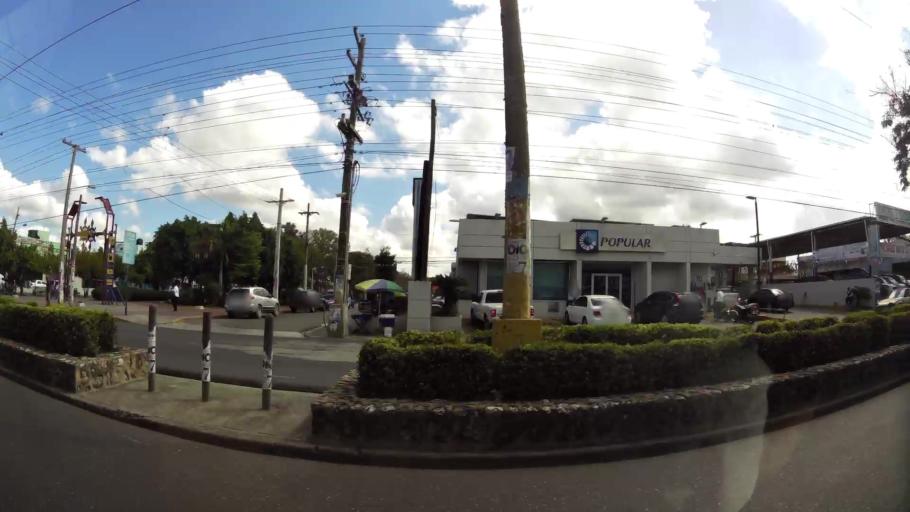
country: DO
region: Santo Domingo
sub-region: Santo Domingo
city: Santo Domingo Este
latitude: 18.5032
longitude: -69.8260
